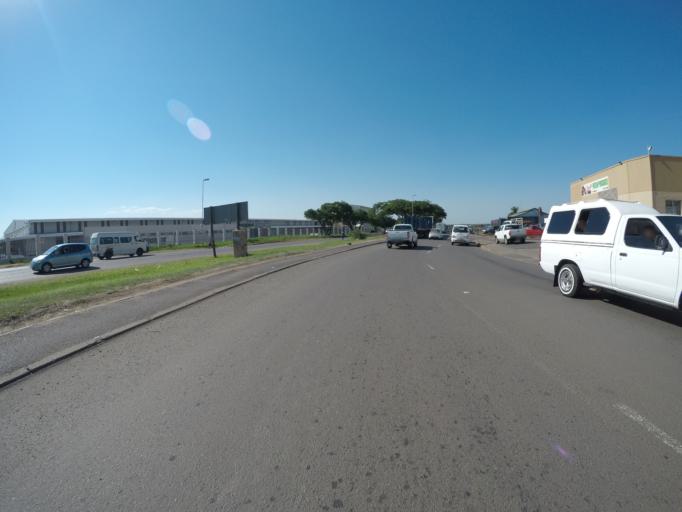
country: ZA
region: KwaZulu-Natal
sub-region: uThungulu District Municipality
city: Empangeni
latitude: -28.7780
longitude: 31.8998
